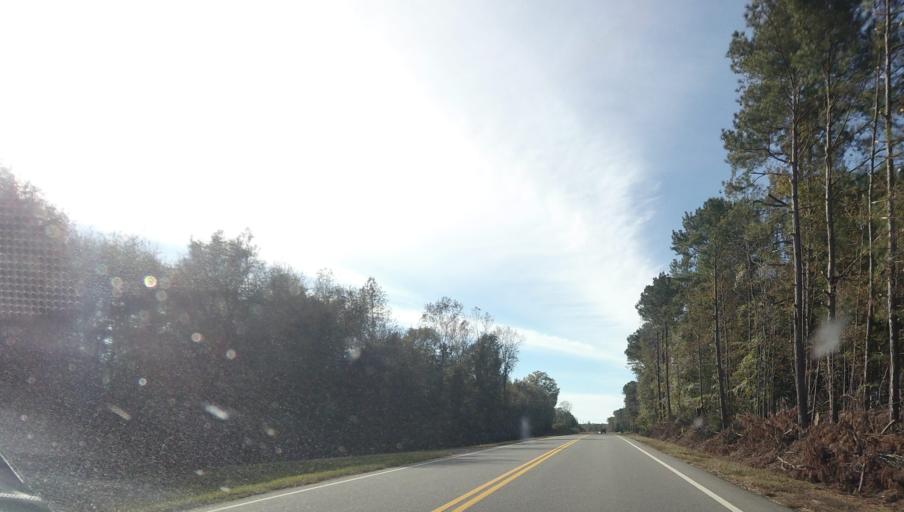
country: US
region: Georgia
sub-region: Upson County
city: Thomaston
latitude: 32.7206
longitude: -84.3163
